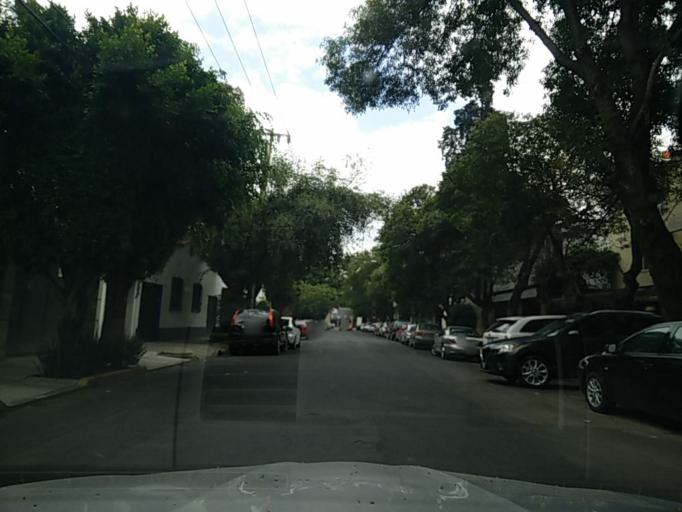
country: MX
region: Mexico City
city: Coyoacan
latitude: 19.3519
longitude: -99.1586
